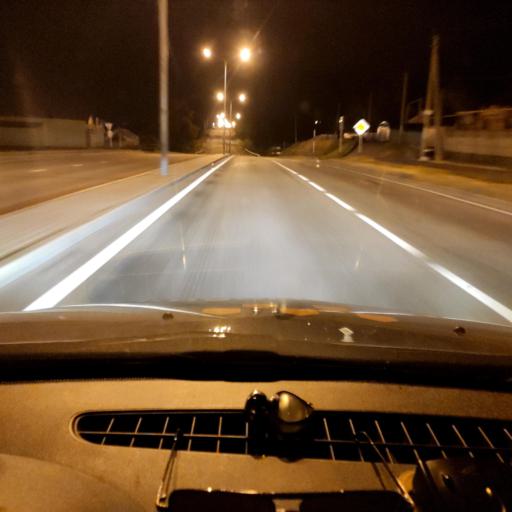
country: RU
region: Belgorod
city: Gubkin
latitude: 51.2676
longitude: 37.5635
